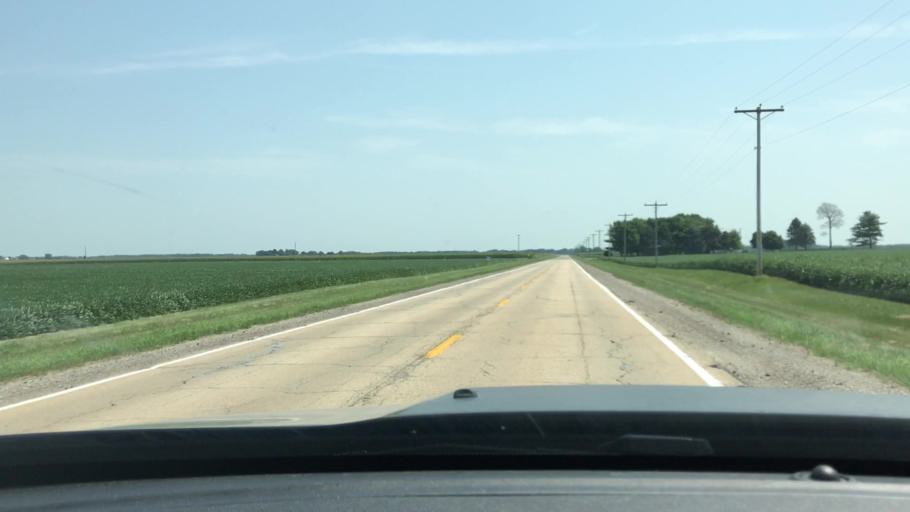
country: US
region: Illinois
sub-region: LaSalle County
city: Sheridan
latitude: 41.4853
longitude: -88.8051
